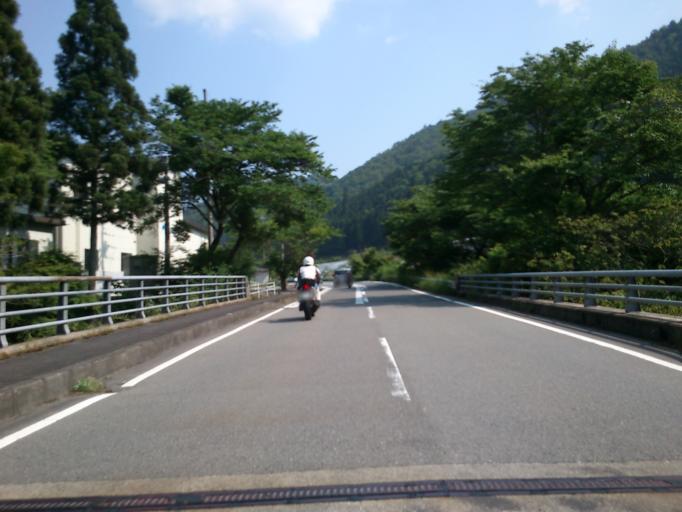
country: JP
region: Kyoto
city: Kameoka
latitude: 35.2374
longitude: 135.5639
